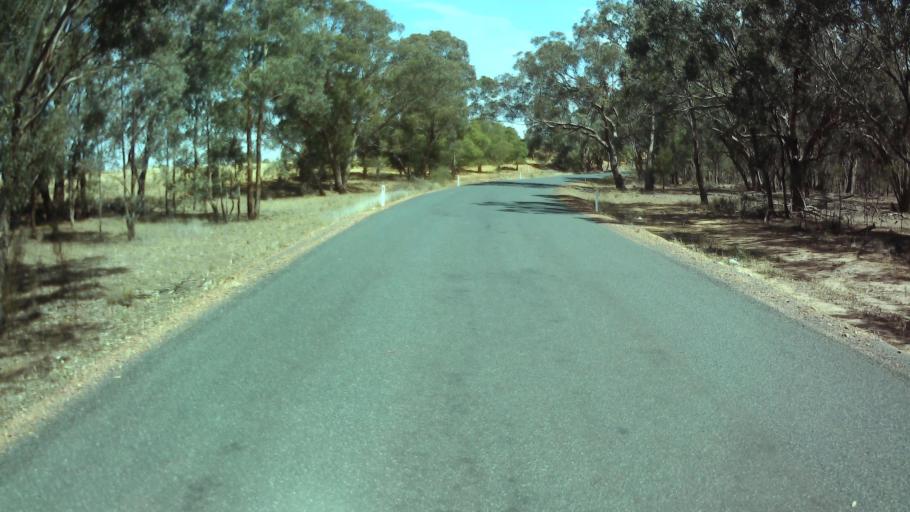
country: AU
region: New South Wales
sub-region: Weddin
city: Grenfell
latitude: -34.0011
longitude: 148.1308
